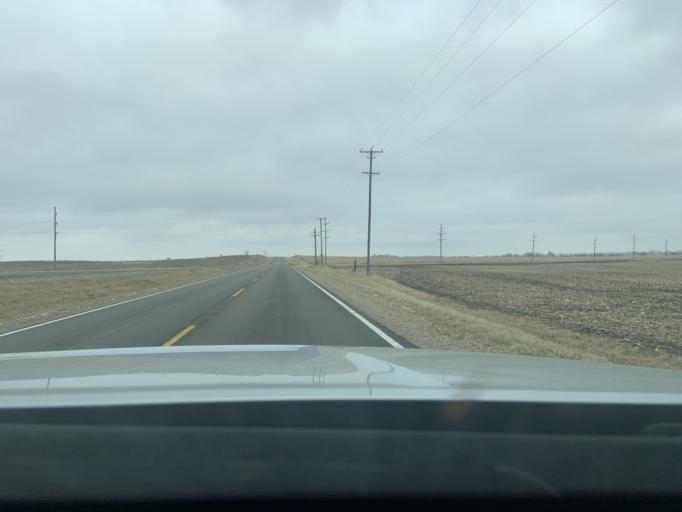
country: US
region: Illinois
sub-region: LaSalle County
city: Sheridan
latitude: 41.4564
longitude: -88.6153
